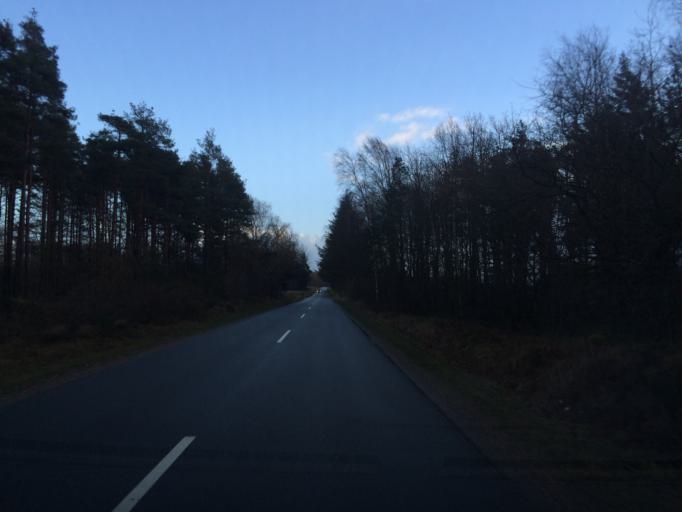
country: DK
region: Central Jutland
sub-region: Holstebro Kommune
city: Ulfborg
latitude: 56.2493
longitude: 8.3730
